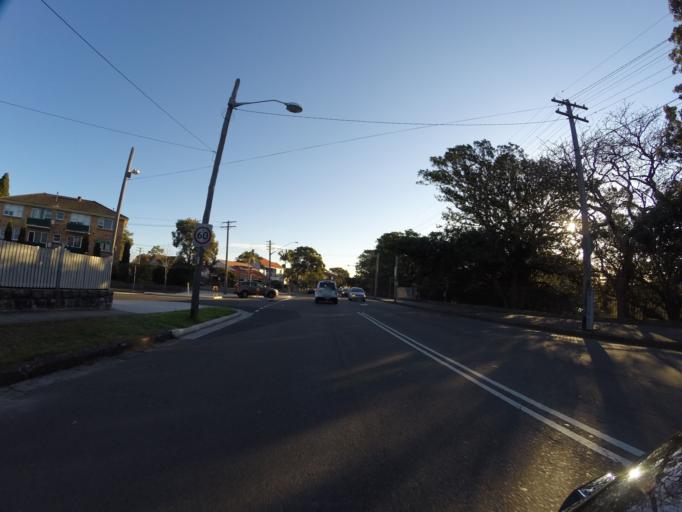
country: AU
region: New South Wales
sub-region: Waverley
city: Bondi Junction
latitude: -33.9027
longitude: 151.2420
